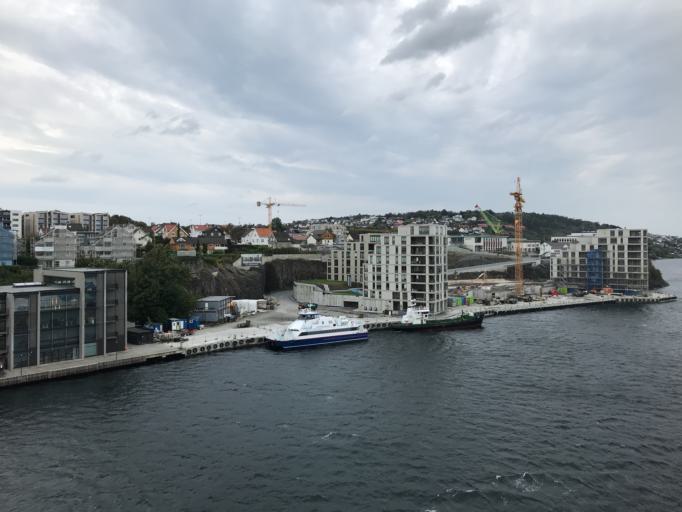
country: NO
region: Rogaland
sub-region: Stavanger
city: Stavanger
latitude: 58.9810
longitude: 5.7206
